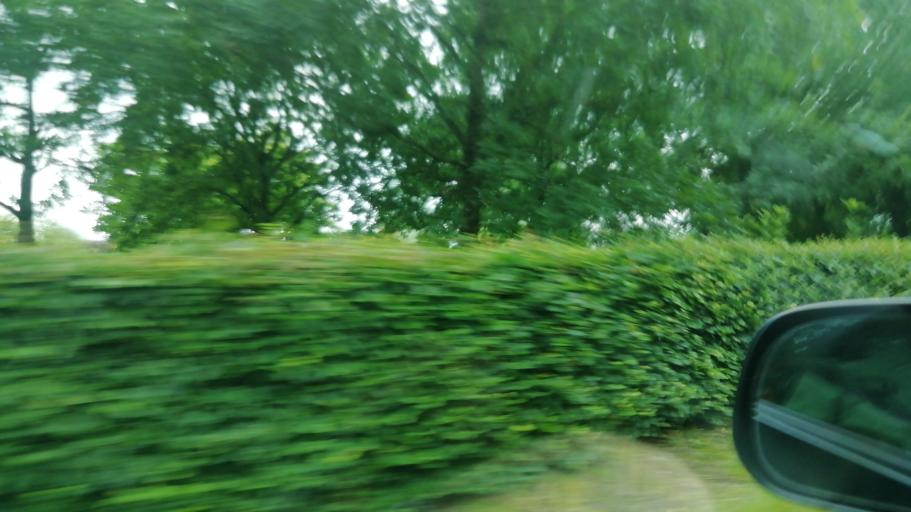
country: IE
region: Munster
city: Fethard
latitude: 52.4954
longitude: -7.6891
